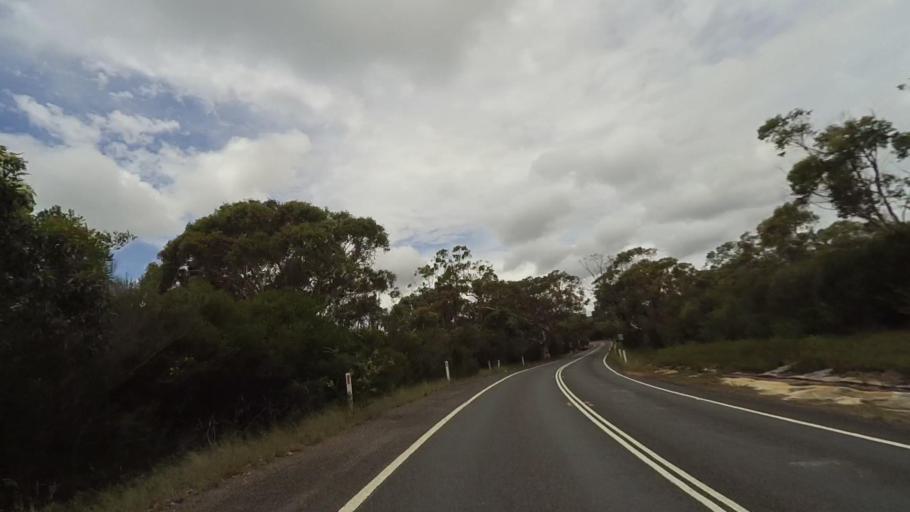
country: AU
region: New South Wales
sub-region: Sutherland Shire
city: Grays Point
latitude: -34.0827
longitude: 151.0634
